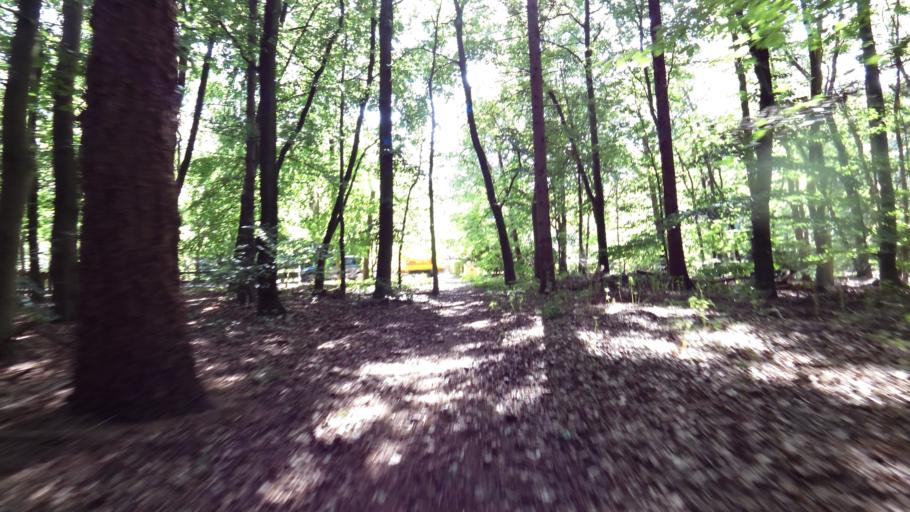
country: NL
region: Gelderland
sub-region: Gemeente Renkum
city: Renkum
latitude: 52.0110
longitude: 5.7143
